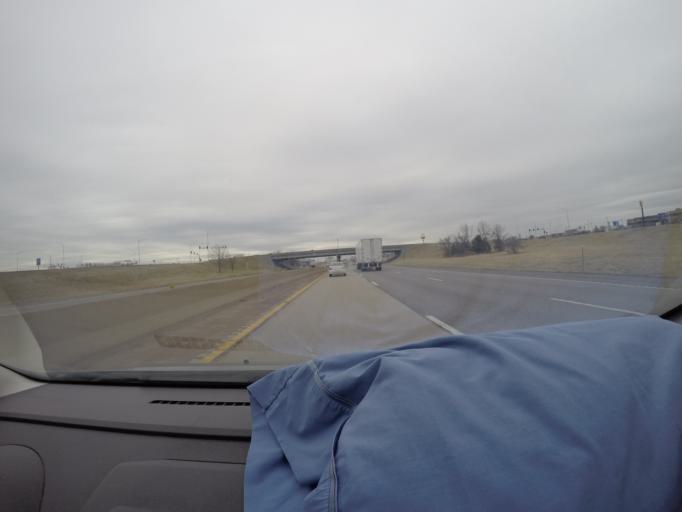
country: US
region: Missouri
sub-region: Saint Charles County
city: Saint Peters
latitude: 38.7943
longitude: -90.5666
